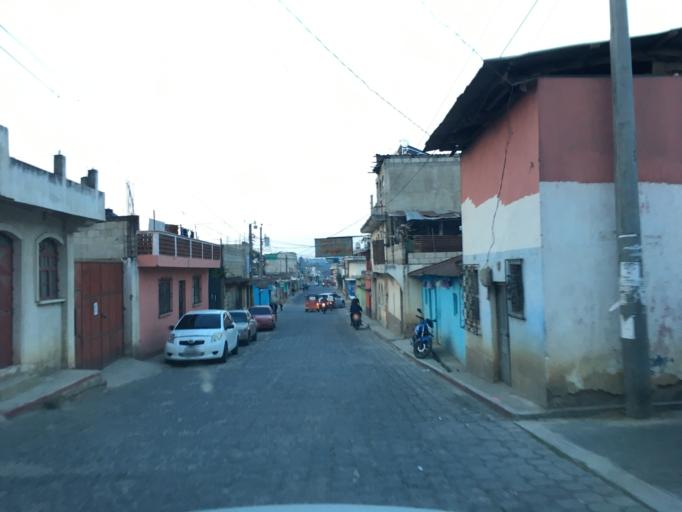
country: GT
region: Chimaltenango
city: Tecpan Guatemala
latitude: 14.7620
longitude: -90.9948
